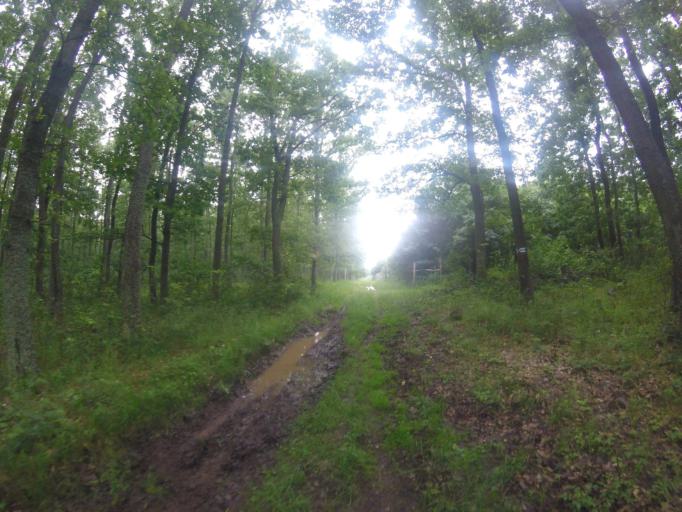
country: HU
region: Veszprem
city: Urkut
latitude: 47.0249
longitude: 17.6618
